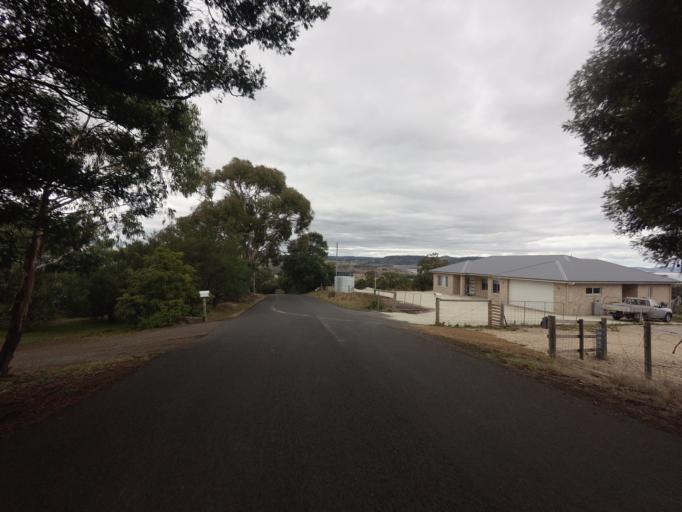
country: AU
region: Tasmania
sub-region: Clarence
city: Cambridge
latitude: -42.7875
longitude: 147.4109
